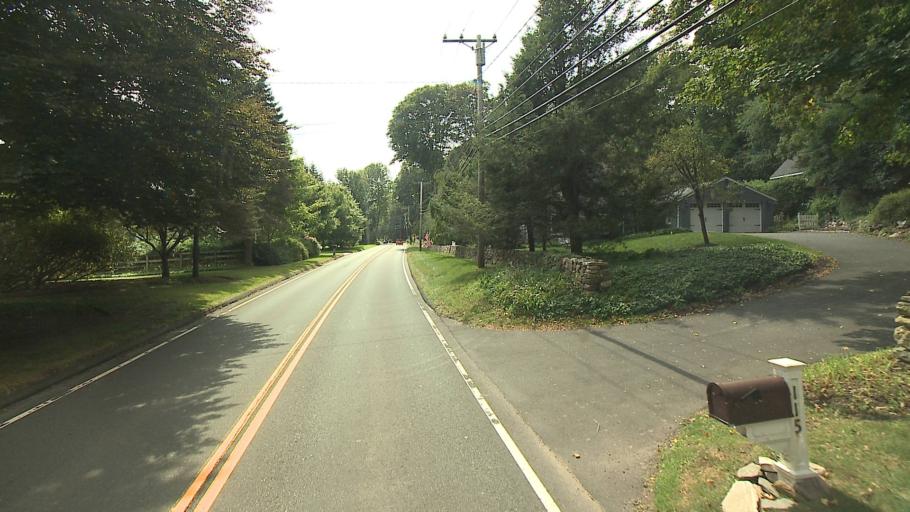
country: US
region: Connecticut
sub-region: Fairfield County
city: Ridgefield
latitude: 41.2955
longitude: -73.5045
